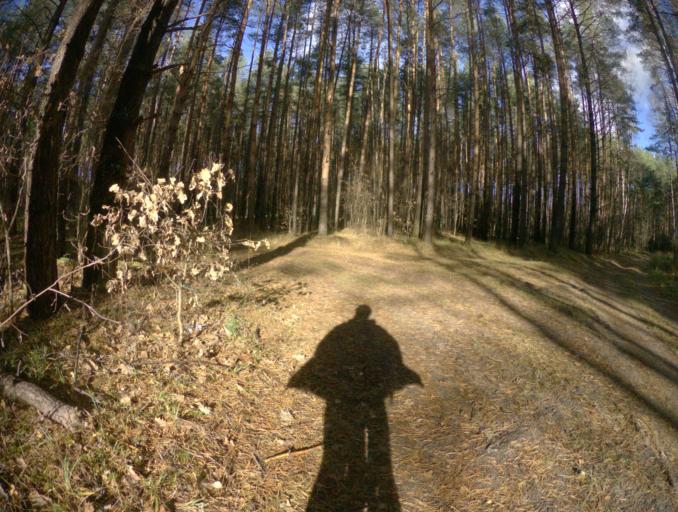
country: RU
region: Vladimir
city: Raduzhnyy
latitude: 56.0600
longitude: 40.3407
